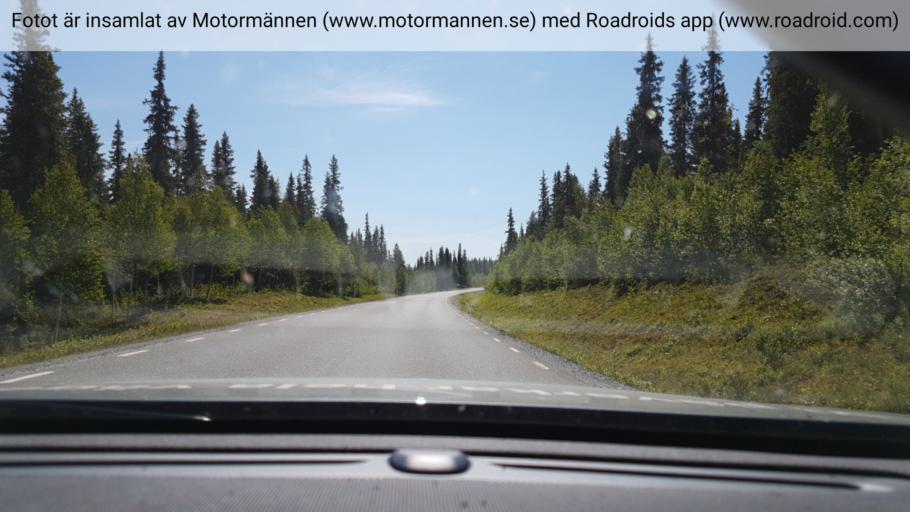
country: SE
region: Vaesterbotten
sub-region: Vilhelmina Kommun
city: Sjoberg
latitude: 64.7860
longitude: 15.3100
